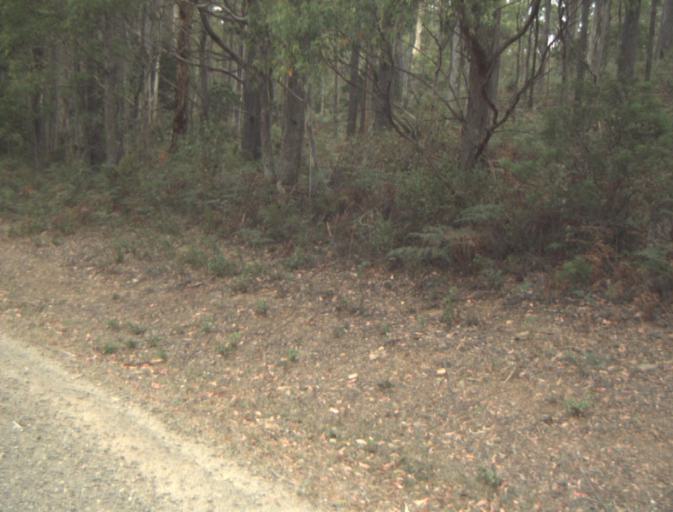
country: AU
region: Tasmania
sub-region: Dorset
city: Scottsdale
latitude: -41.4305
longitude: 147.5141
